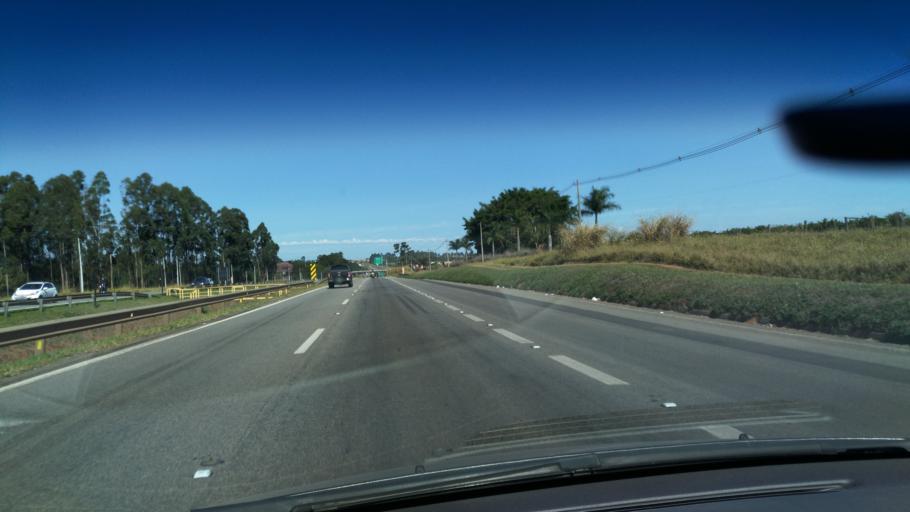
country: BR
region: Sao Paulo
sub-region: Santo Antonio De Posse
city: Santo Antonio de Posse
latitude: -22.6111
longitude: -47.0074
